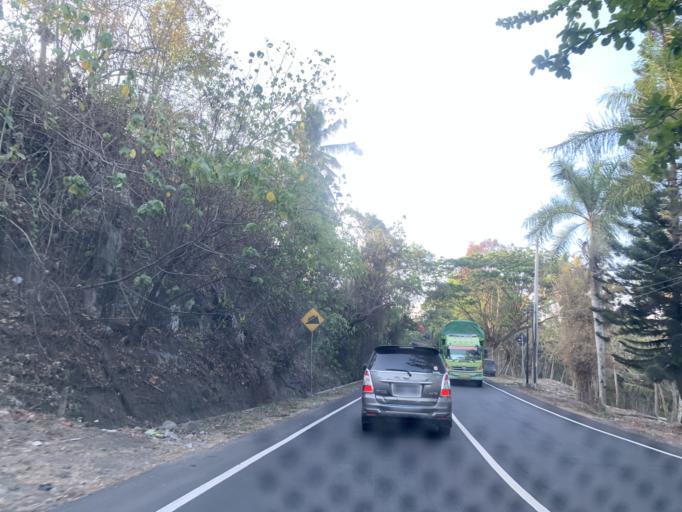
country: ID
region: Bali
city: Banjar Delodrurung
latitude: -8.4985
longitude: 114.9671
